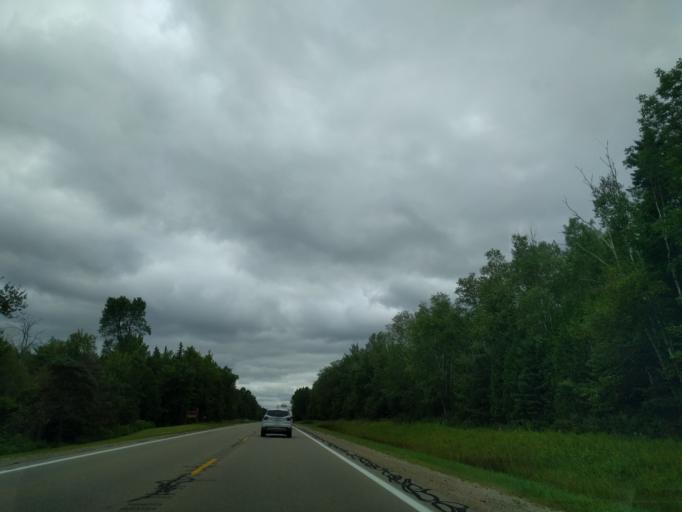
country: US
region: Michigan
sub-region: Menominee County
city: Menominee
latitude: 45.3449
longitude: -87.4109
